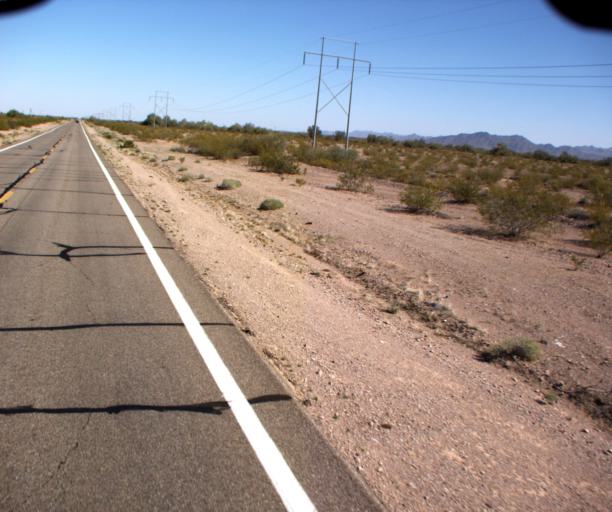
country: US
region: Arizona
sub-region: La Paz County
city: Quartzsite
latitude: 33.4887
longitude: -114.2170
